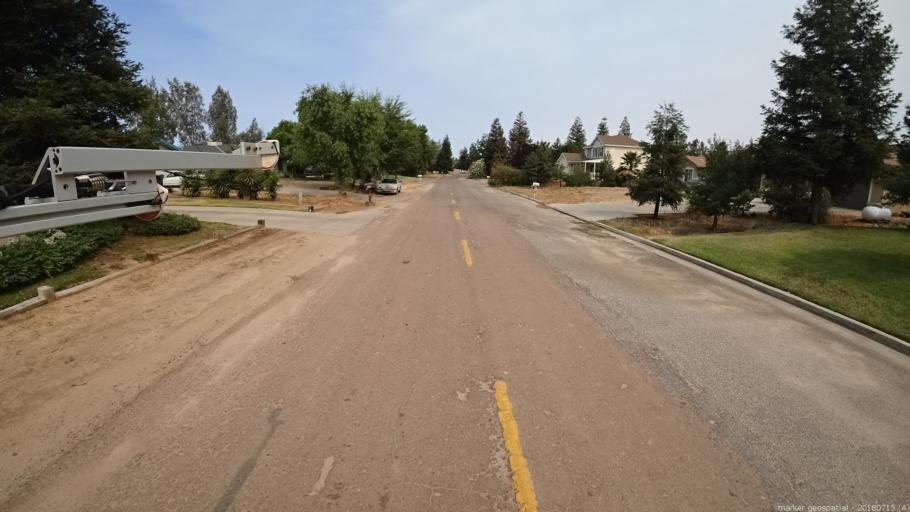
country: US
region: California
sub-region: Madera County
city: Madera Acres
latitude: 37.0197
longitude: -120.0705
